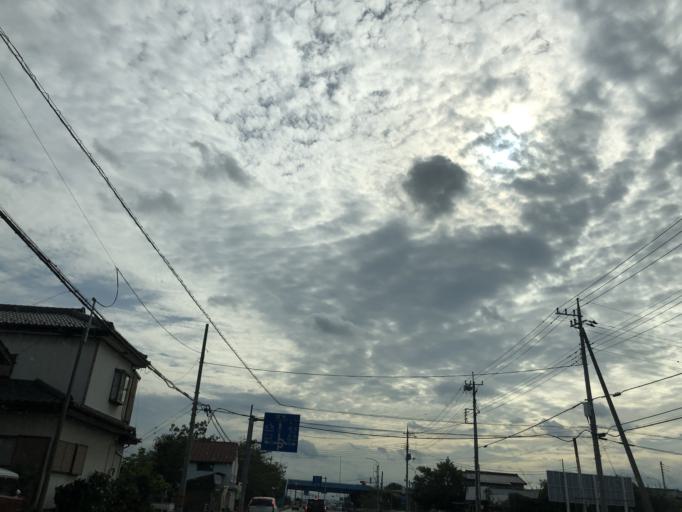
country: JP
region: Tochigi
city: Sano
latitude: 36.2898
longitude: 139.5642
